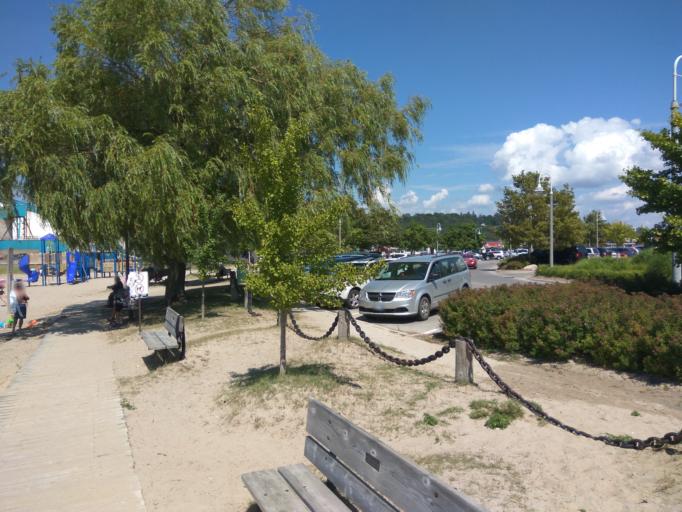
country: CA
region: Ontario
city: Goderich
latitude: 43.7439
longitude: -81.7260
